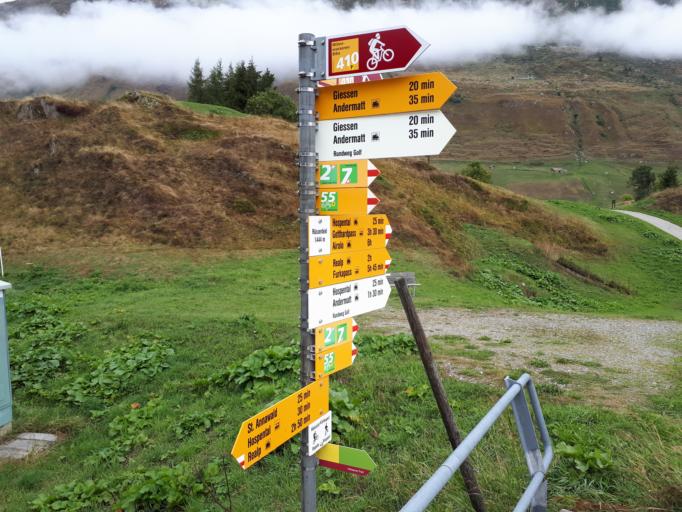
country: CH
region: Uri
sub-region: Uri
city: Andermatt
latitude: 46.6274
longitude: 8.5797
